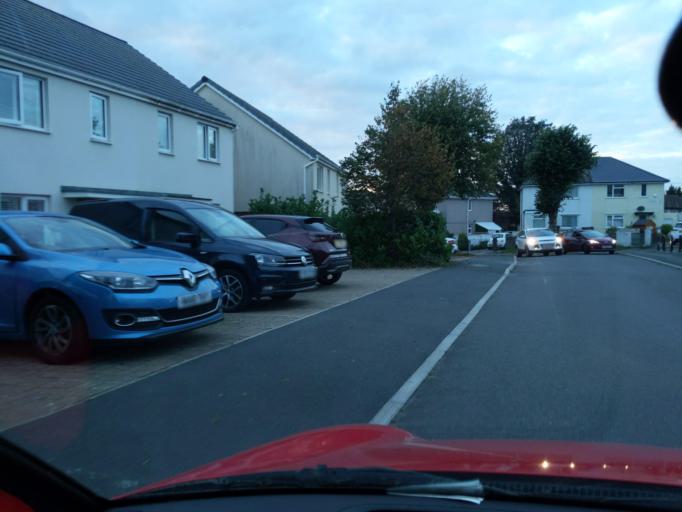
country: GB
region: England
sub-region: Cornwall
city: Millbrook
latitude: 50.3944
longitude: -4.1694
